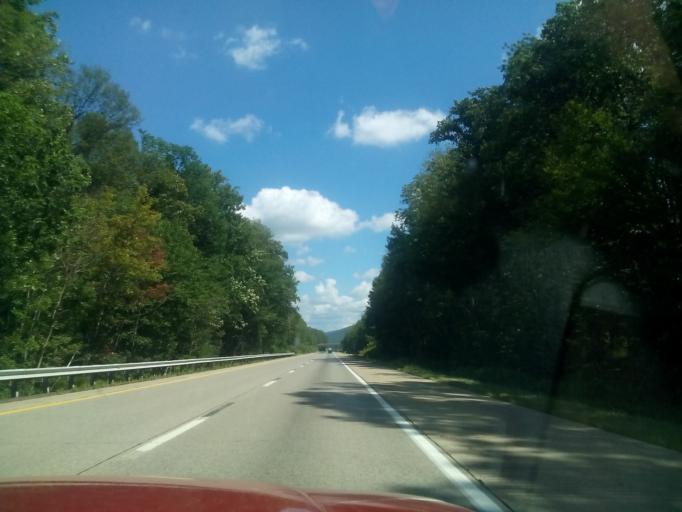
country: US
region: Pennsylvania
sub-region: Luzerne County
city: Nescopeck
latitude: 41.0141
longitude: -76.2133
